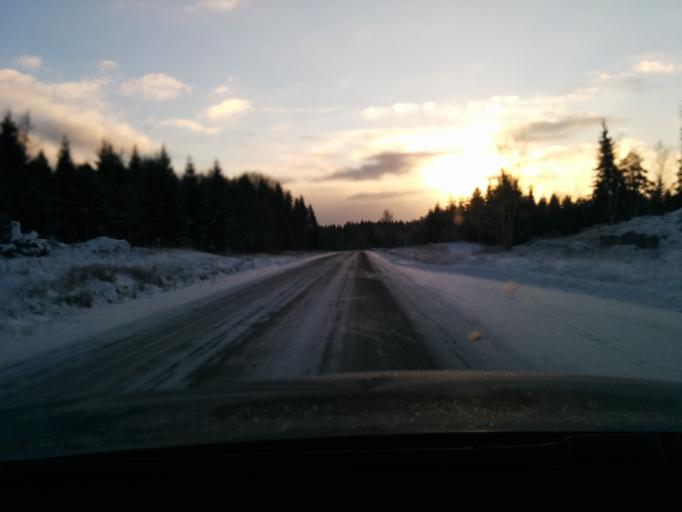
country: SE
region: Uppsala
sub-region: Tierps Kommun
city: Orbyhus
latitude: 60.2098
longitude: 17.6988
